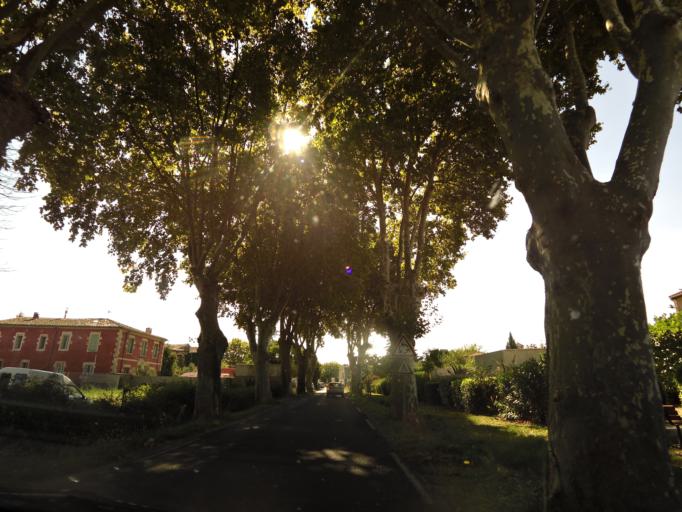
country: FR
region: Languedoc-Roussillon
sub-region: Departement du Gard
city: Vestric-et-Candiac
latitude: 43.7423
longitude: 4.2589
